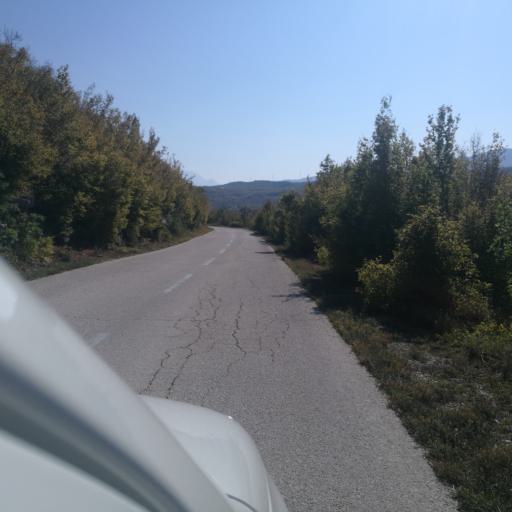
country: HR
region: Splitsko-Dalmatinska
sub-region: Grad Omis
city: Omis
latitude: 43.5214
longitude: 16.7523
